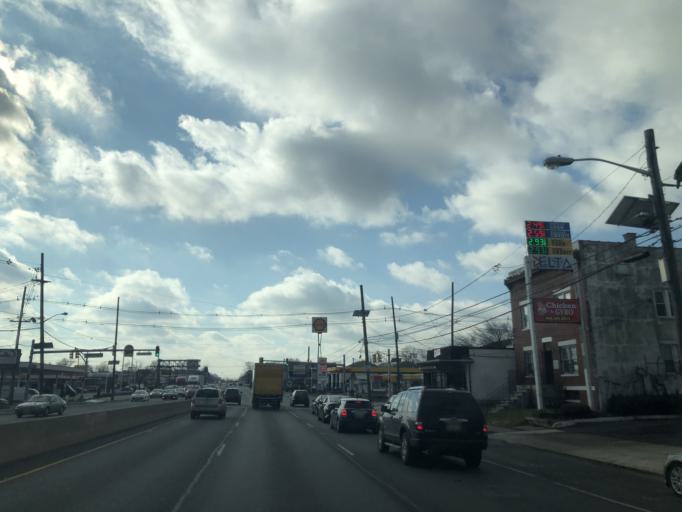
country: US
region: New Jersey
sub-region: Union County
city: Elizabeth
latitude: 40.6745
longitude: -74.1995
